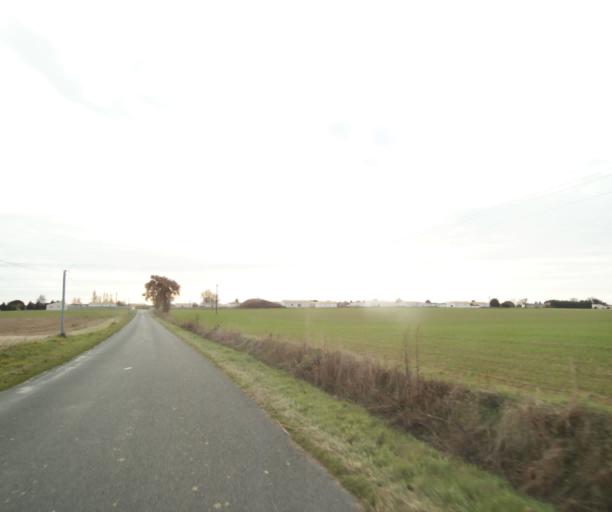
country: FR
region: Poitou-Charentes
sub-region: Departement de la Charente-Maritime
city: Corme-Royal
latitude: 45.7515
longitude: -0.8055
